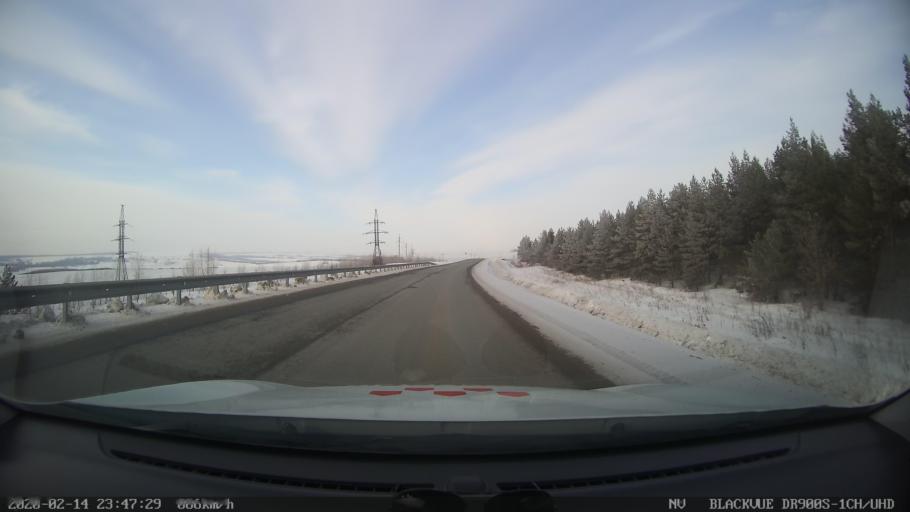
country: RU
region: Tatarstan
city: Kuybyshevskiy Zaton
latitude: 55.2391
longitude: 49.2085
